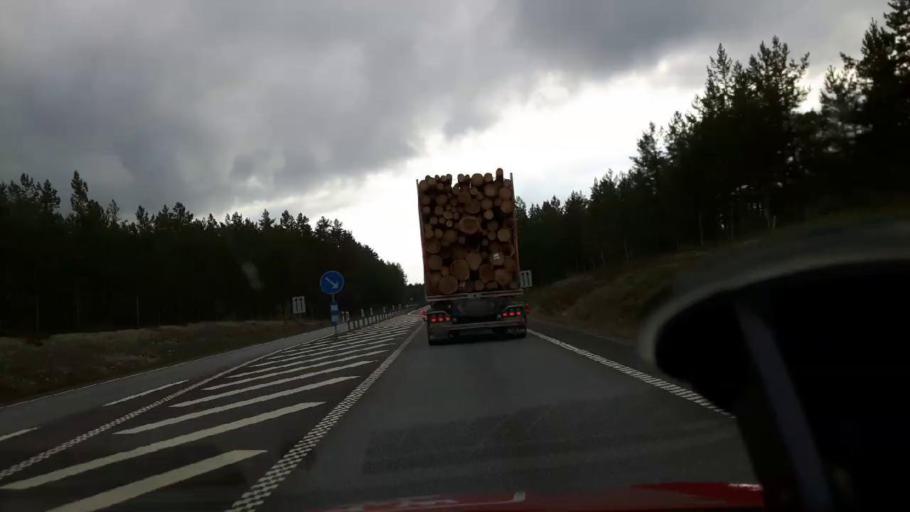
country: SE
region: Gaevleborg
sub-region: Gavle Kommun
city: Norrsundet
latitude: 61.0231
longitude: 16.9762
